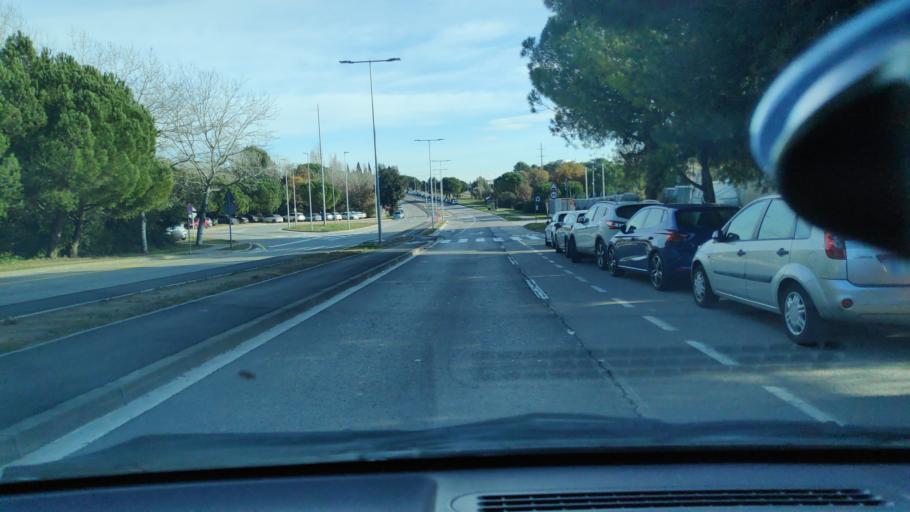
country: ES
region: Catalonia
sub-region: Provincia de Barcelona
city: Rubi
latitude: 41.4918
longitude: 2.0574
